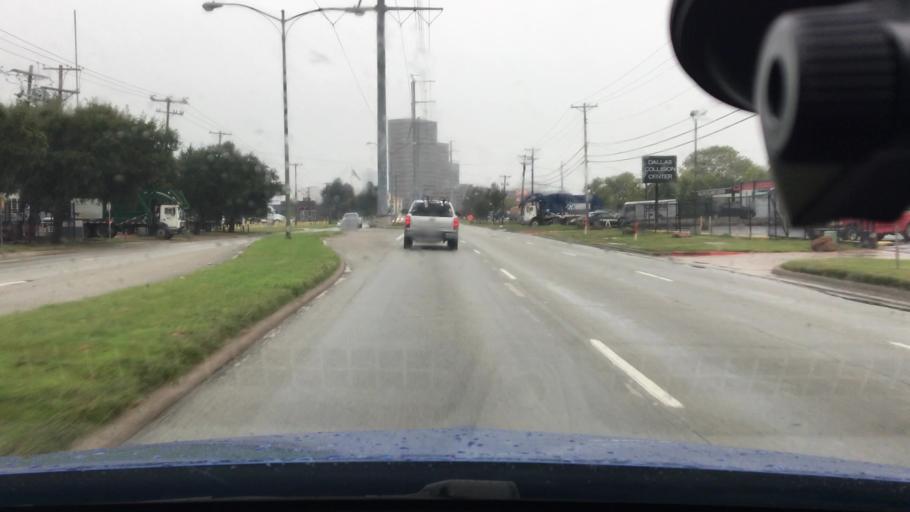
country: US
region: Texas
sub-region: Dallas County
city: Dallas
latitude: 32.8085
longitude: -96.8576
